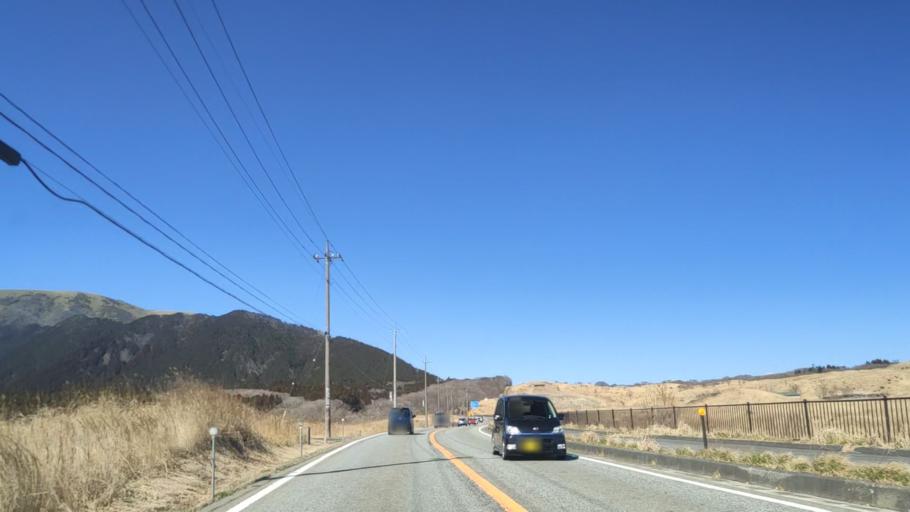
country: JP
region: Yamanashi
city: Fujikawaguchiko
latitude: 35.4206
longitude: 138.5914
